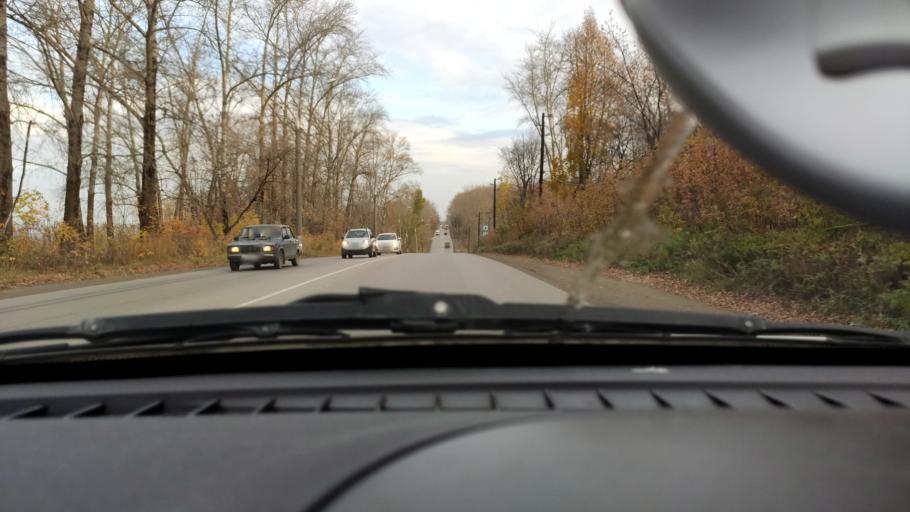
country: RU
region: Perm
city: Perm
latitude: 58.1222
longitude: 56.3697
